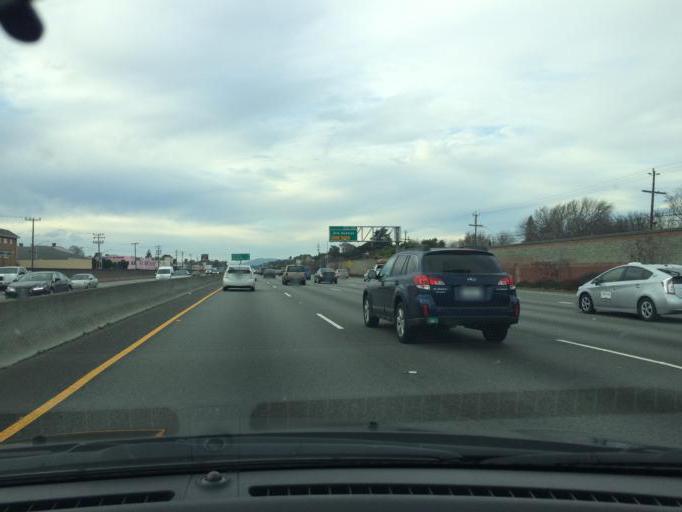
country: US
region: California
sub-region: San Mateo County
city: San Mateo
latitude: 37.5647
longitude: -122.3073
